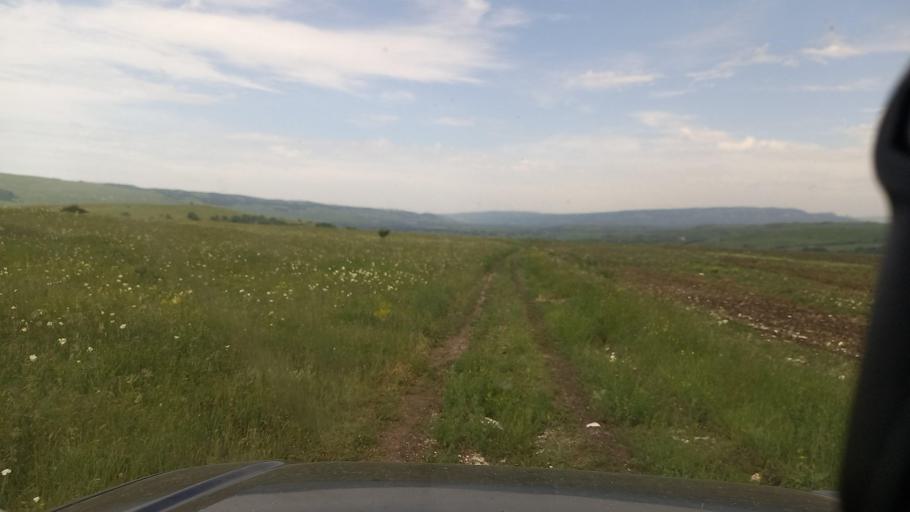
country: RU
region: Krasnodarskiy
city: Peredovaya
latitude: 44.0768
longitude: 41.3272
